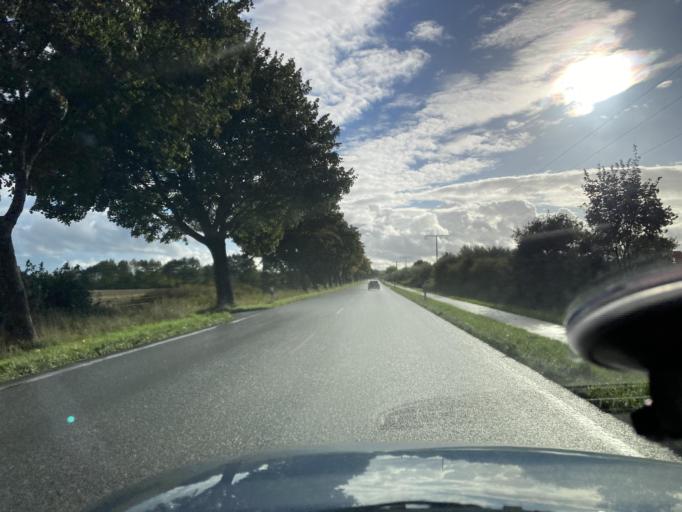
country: DE
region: Schleswig-Holstein
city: Fockbek
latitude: 54.2952
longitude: 9.5870
